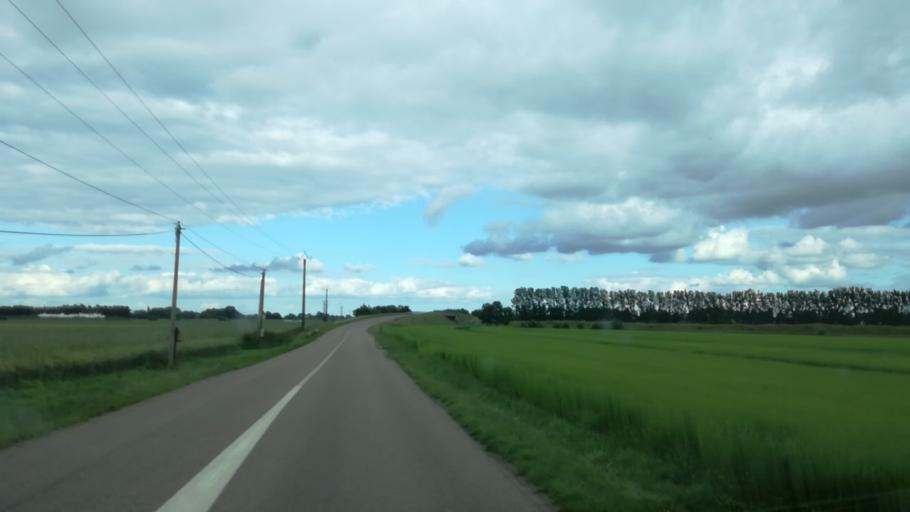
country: FR
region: Haute-Normandie
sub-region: Departement de l'Eure
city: Bourg-Achard
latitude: 49.3028
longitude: 0.7950
